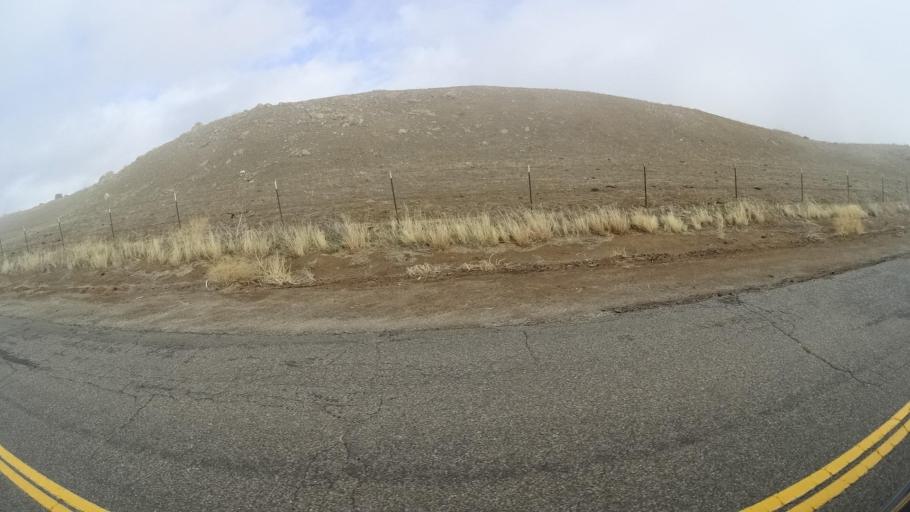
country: US
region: California
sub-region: Kern County
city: Maricopa
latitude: 34.9282
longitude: -119.4097
